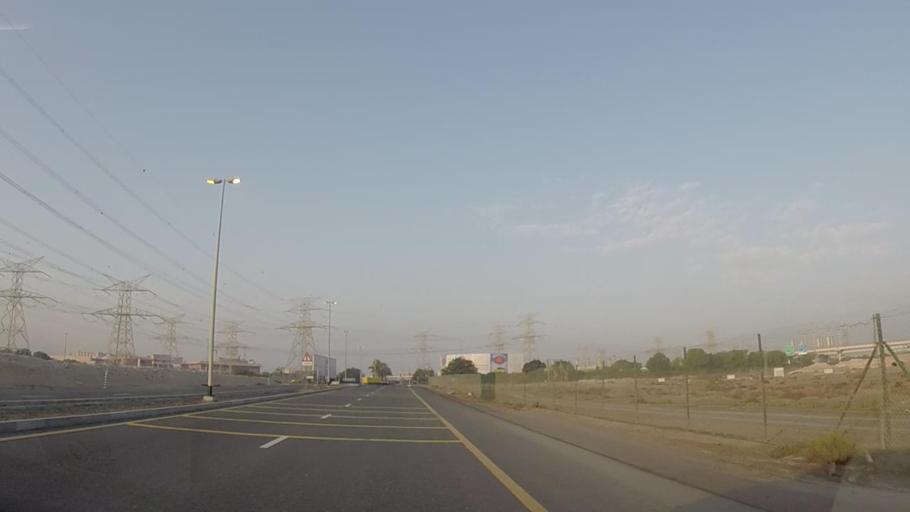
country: AE
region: Dubai
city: Dubai
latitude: 25.0533
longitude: 55.1246
